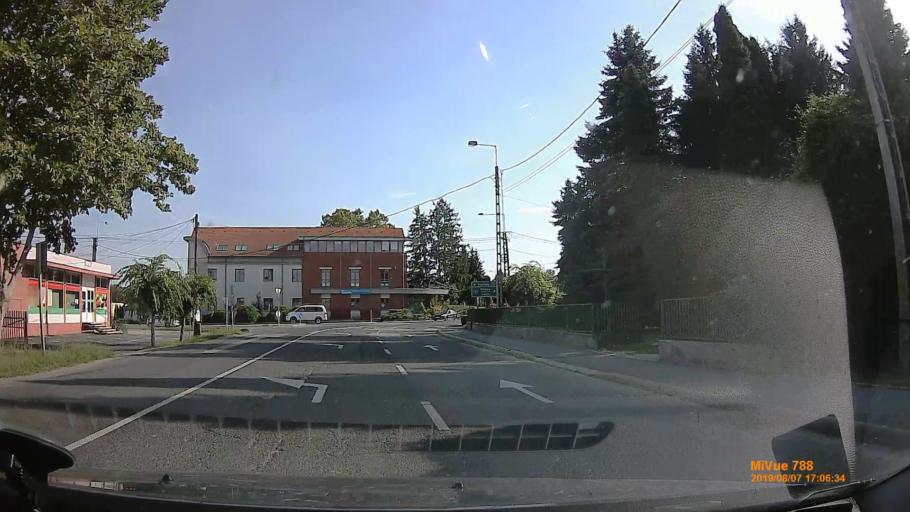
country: HU
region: Zala
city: Zalaegerszeg
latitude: 46.7312
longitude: 16.8463
